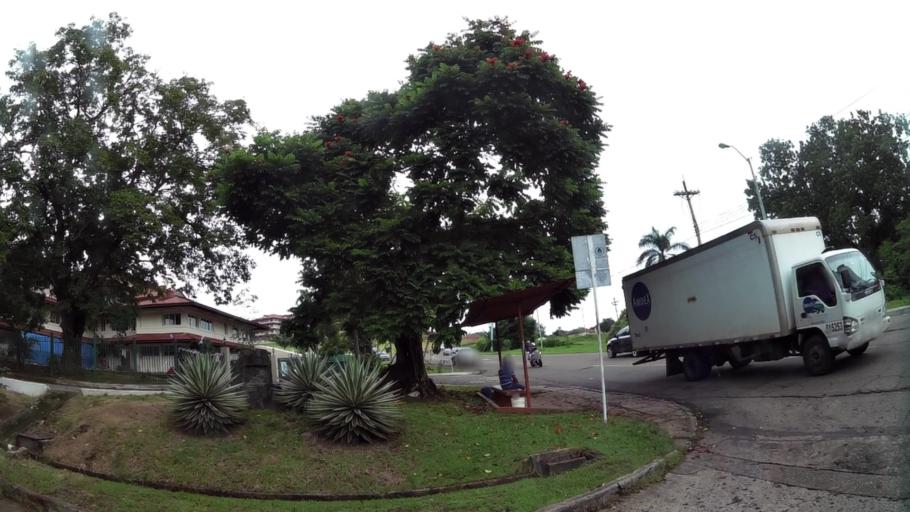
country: PA
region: Panama
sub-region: Distrito de Panama
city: Ancon
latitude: 9.0057
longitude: -79.5688
